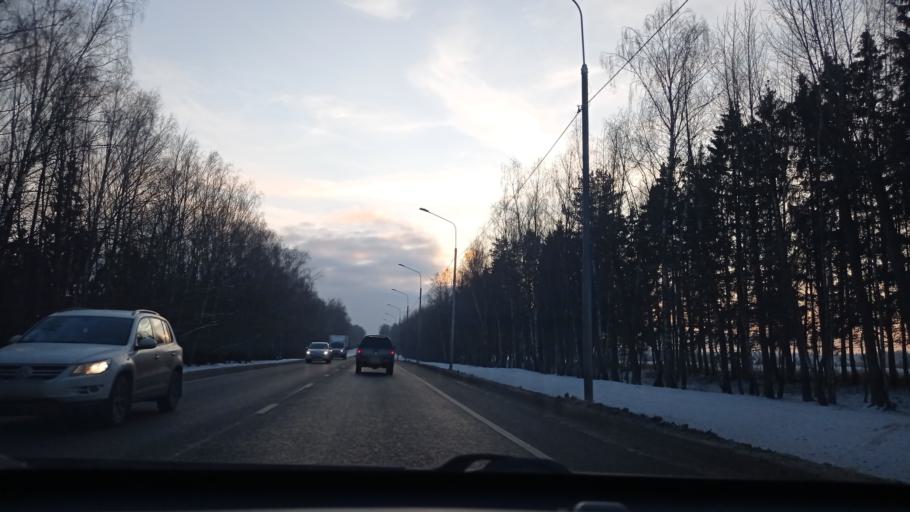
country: RU
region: Moskovskaya
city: Troitsk
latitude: 55.2981
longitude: 37.1359
